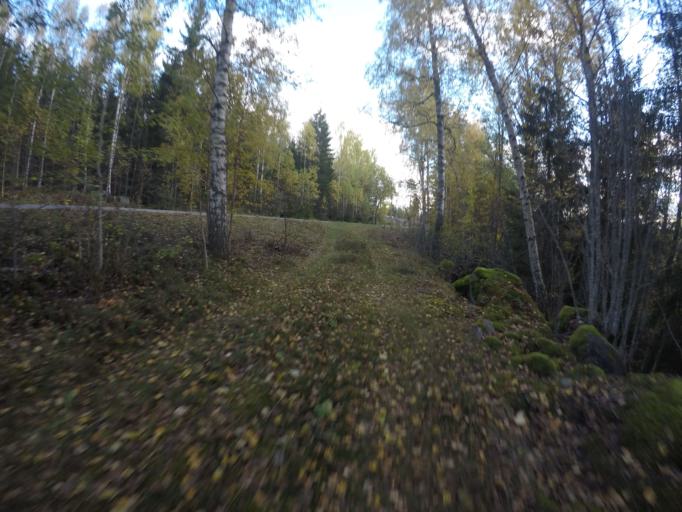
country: SE
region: Vaestmanland
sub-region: Arboga Kommun
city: Tyringe
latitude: 59.3388
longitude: 15.9631
